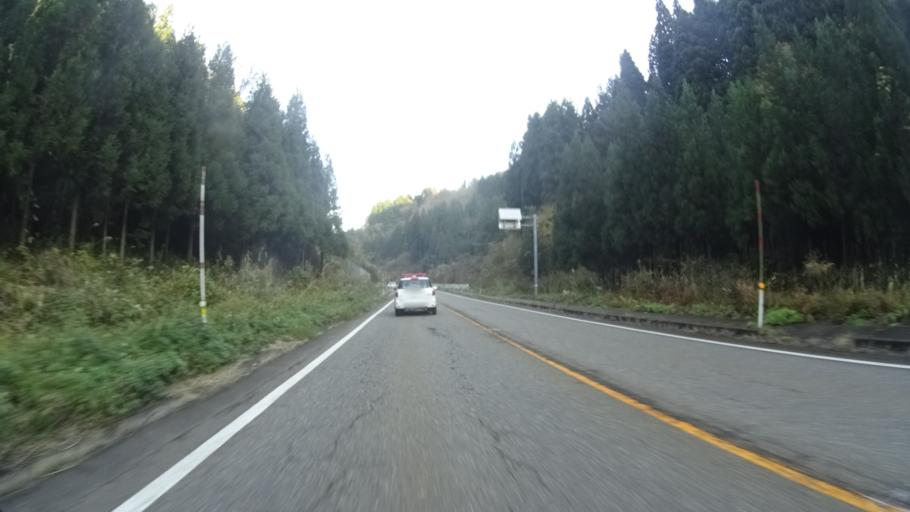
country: JP
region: Niigata
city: Kashiwazaki
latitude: 37.4123
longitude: 138.6760
